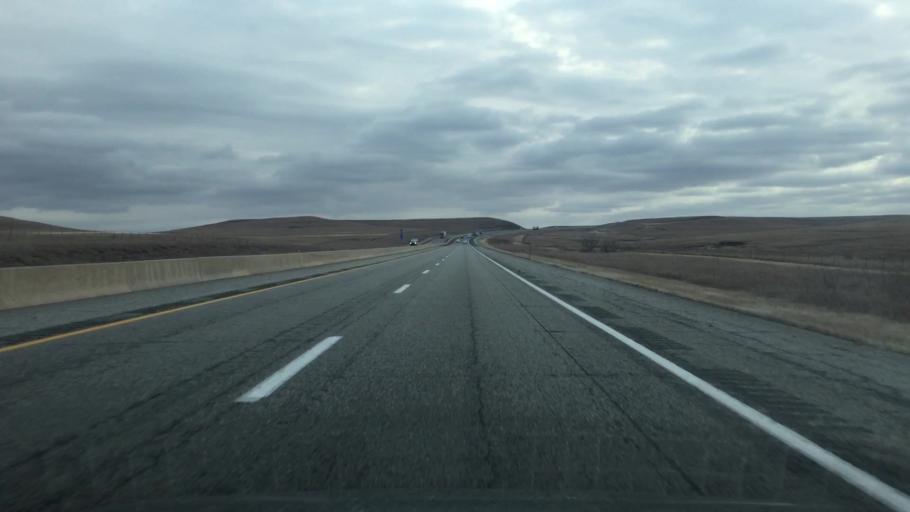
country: US
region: Kansas
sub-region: Chase County
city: Cottonwood Falls
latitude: 38.2484
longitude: -96.3937
